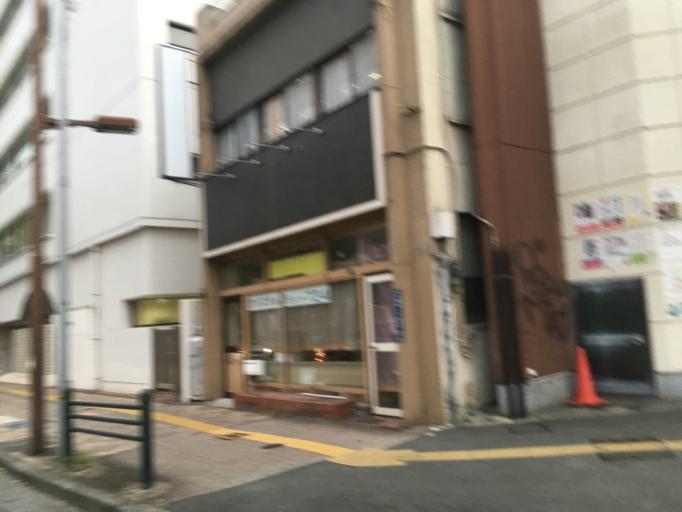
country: JP
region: Kumamoto
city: Kumamoto
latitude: 32.7996
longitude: 130.7175
